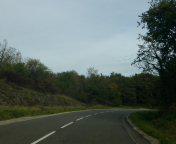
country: FR
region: Bourgogne
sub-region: Departement de Saone-et-Loire
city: Cuiseaux
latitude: 46.4617
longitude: 5.4365
